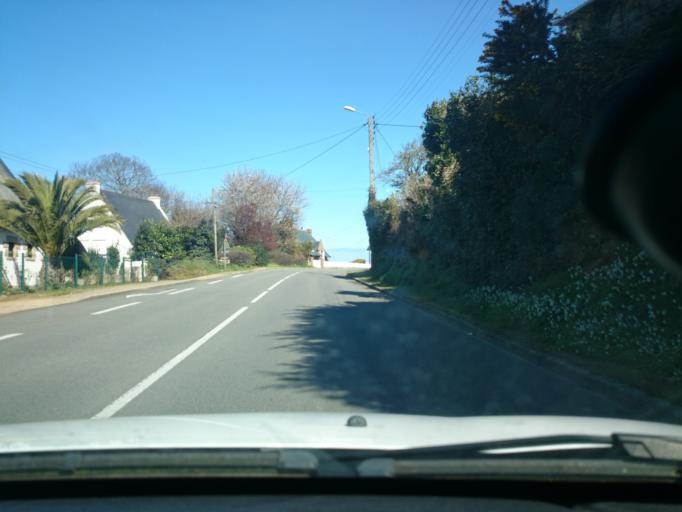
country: FR
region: Brittany
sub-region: Departement des Cotes-d'Armor
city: Perros-Guirec
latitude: 48.8107
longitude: -3.4617
